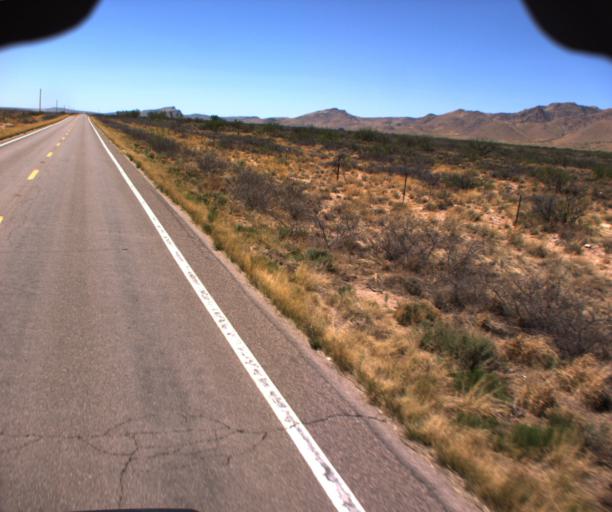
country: US
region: Arizona
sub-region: Cochise County
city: Douglas
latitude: 31.7652
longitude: -109.0809
